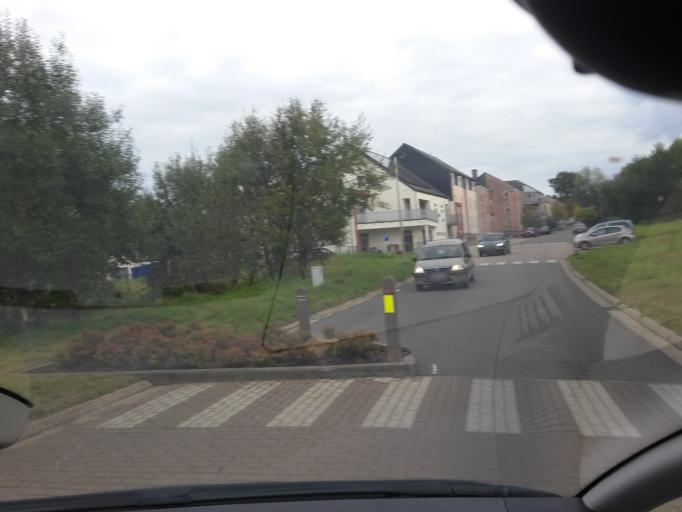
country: BE
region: Wallonia
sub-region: Province du Luxembourg
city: Arlon
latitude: 49.6933
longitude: 5.8058
